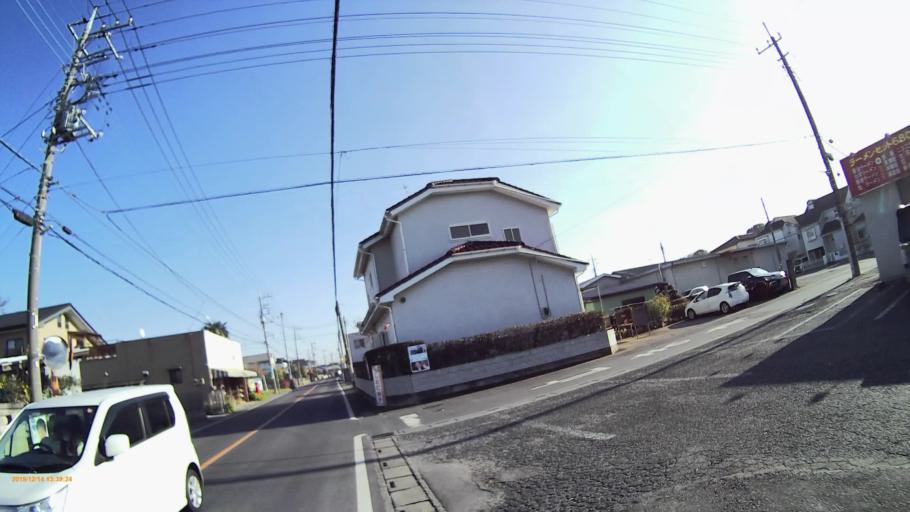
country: JP
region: Saitama
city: Konosu
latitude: 36.0740
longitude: 139.4895
